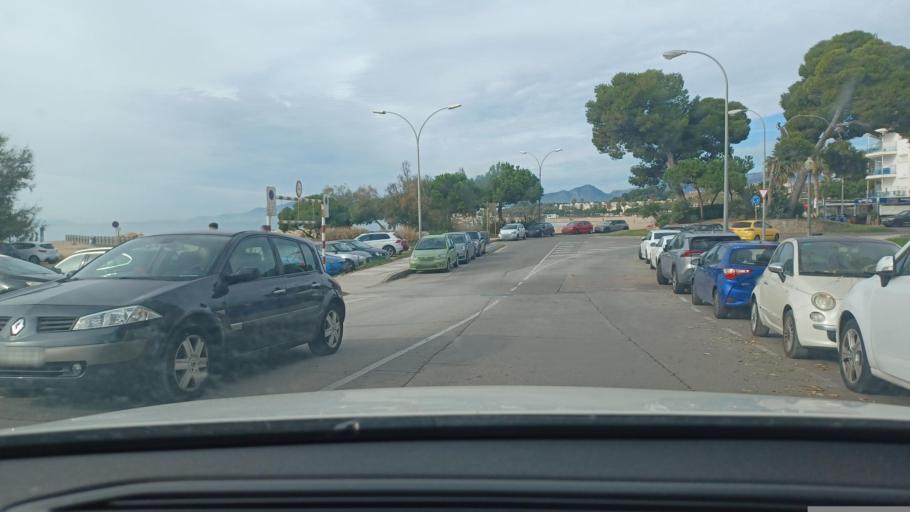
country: ES
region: Catalonia
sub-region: Provincia de Tarragona
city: Cambrils
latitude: 41.0644
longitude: 1.0549
